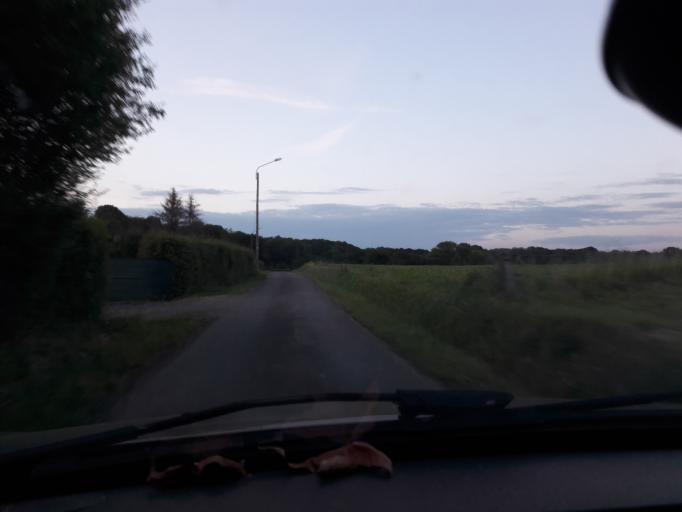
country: BE
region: Wallonia
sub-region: Province du Hainaut
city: Beaumont
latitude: 50.2661
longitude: 4.1883
